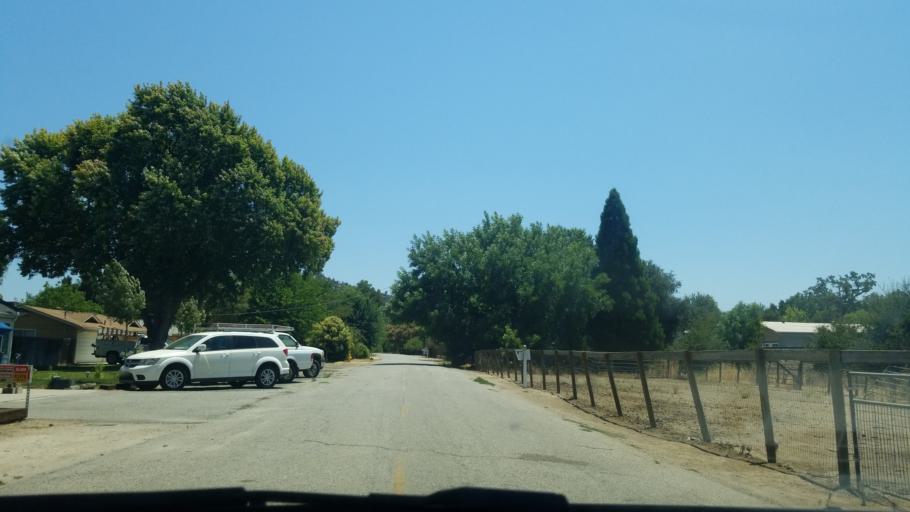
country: US
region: California
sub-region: San Luis Obispo County
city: Atascadero
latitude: 35.5044
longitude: -120.6652
